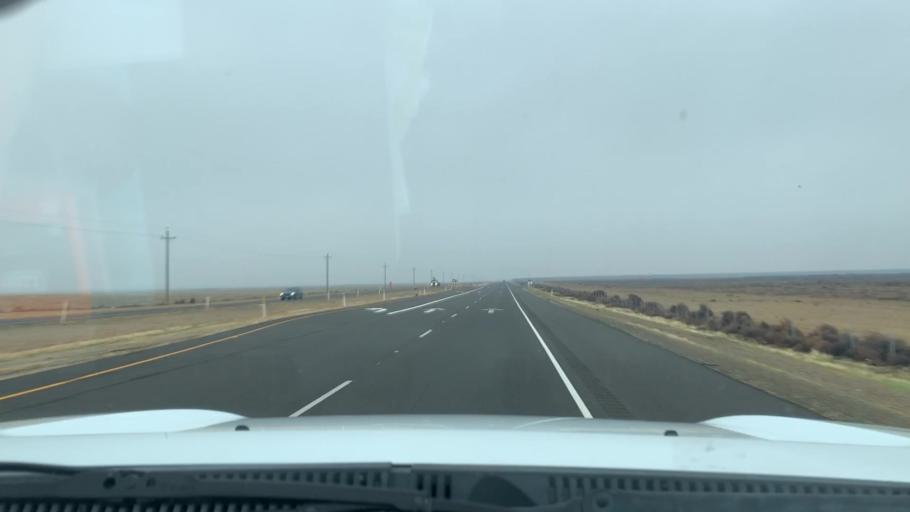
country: US
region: California
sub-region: Kern County
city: Lost Hills
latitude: 35.6156
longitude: -119.7781
